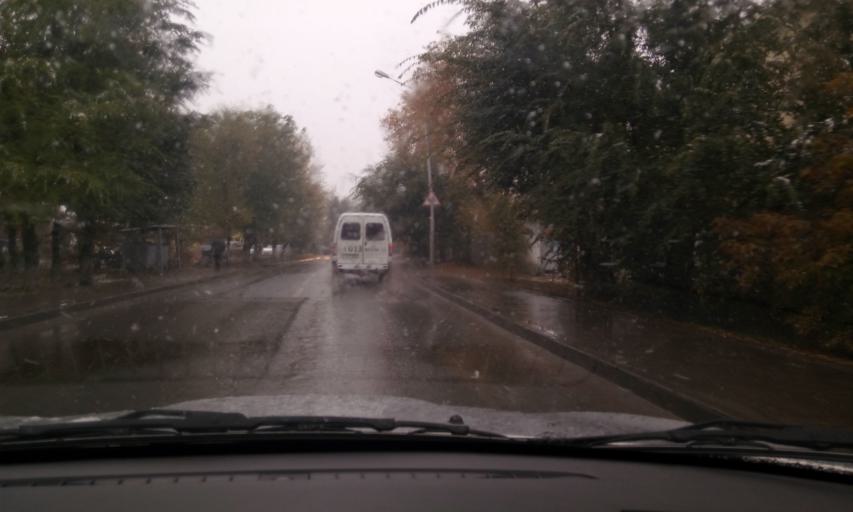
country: KZ
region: Astana Qalasy
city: Astana
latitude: 51.1446
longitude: 71.4300
